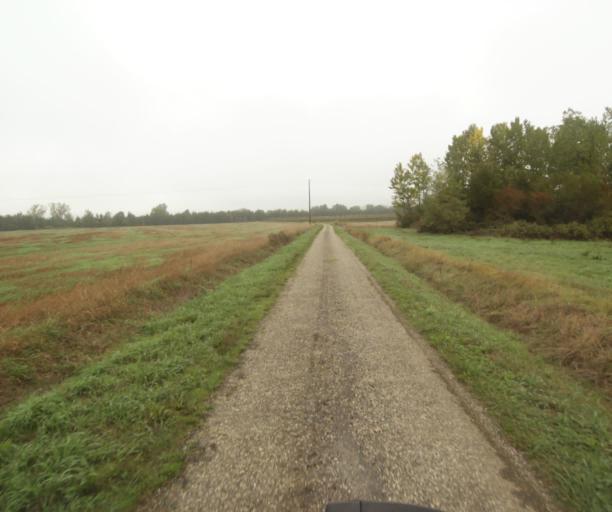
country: FR
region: Midi-Pyrenees
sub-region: Departement du Tarn-et-Garonne
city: Orgueil
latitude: 43.9082
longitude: 1.4172
